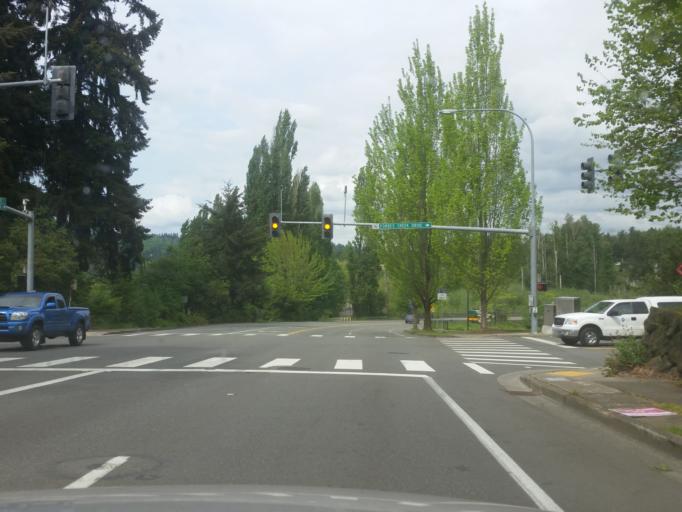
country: US
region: Washington
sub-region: King County
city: Kirkland
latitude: 47.6949
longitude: -122.2100
